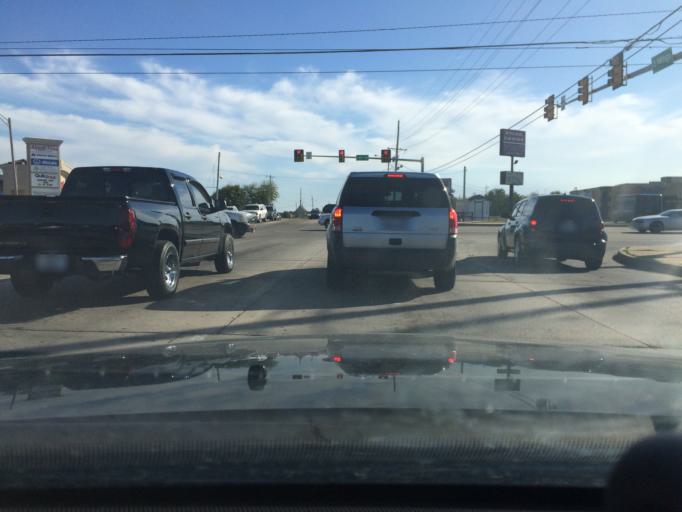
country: US
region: Oklahoma
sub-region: Tulsa County
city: Broken Arrow
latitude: 36.0758
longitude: -95.8686
